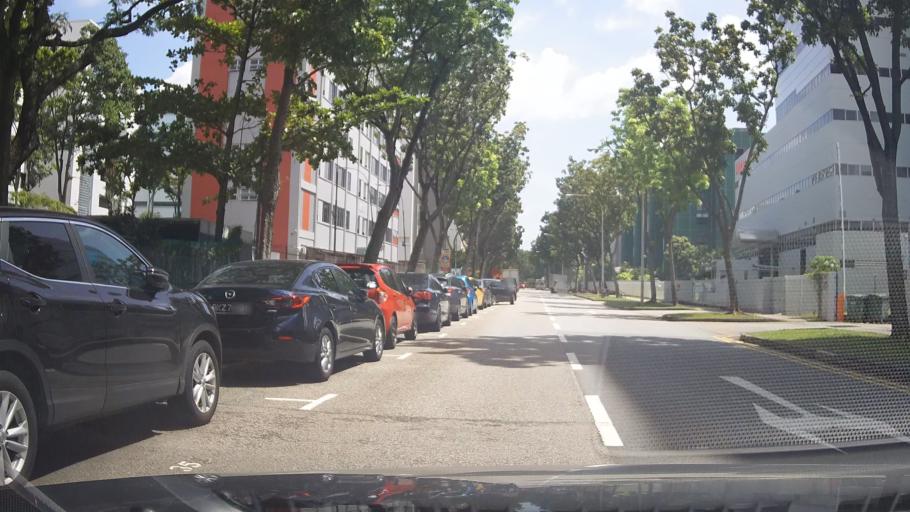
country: SG
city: Singapore
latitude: 1.3100
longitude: 103.8659
